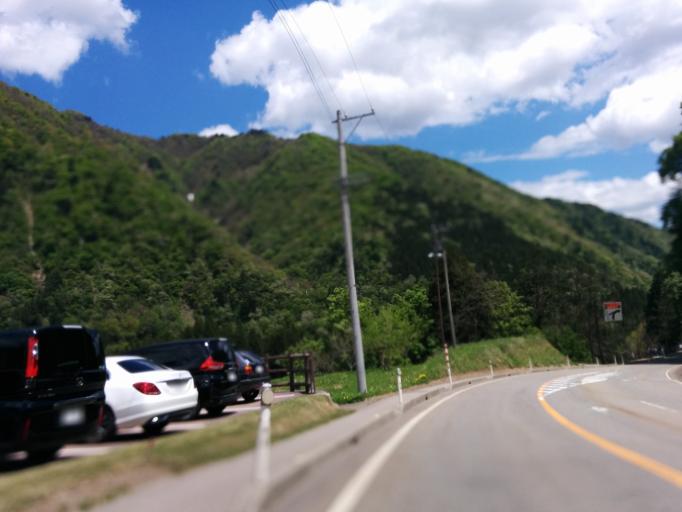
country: JP
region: Toyama
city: Fukumitsu
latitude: 36.4034
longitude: 136.8853
